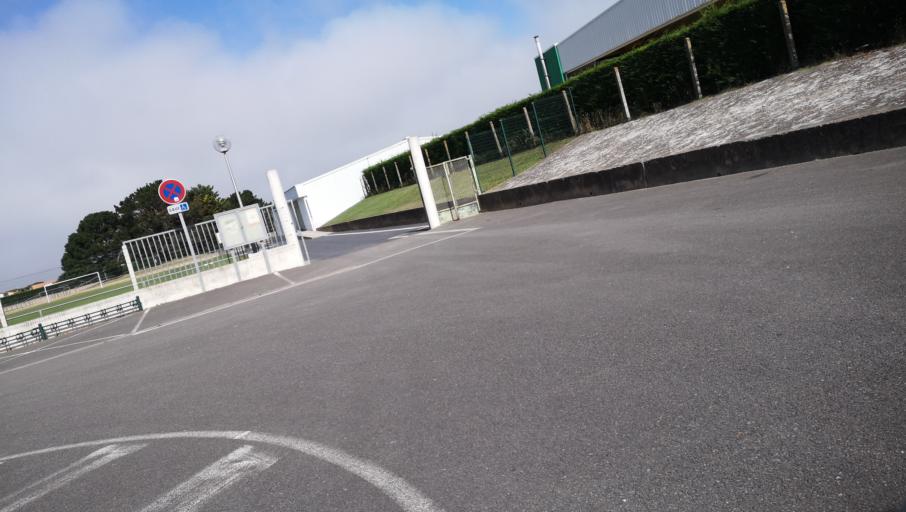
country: FR
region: Pays de la Loire
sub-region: Departement de la Vendee
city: Les Sables-d'Olonne
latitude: 46.5105
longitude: -1.7729
